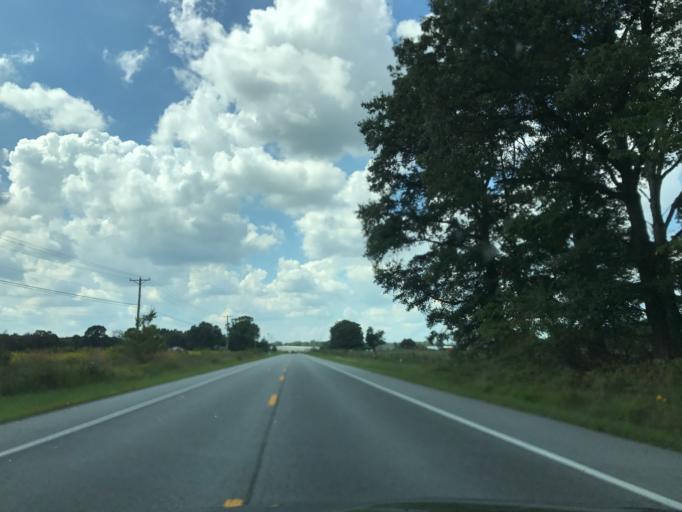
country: US
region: Maryland
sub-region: Caroline County
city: Greensboro
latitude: 39.1434
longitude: -75.8470
